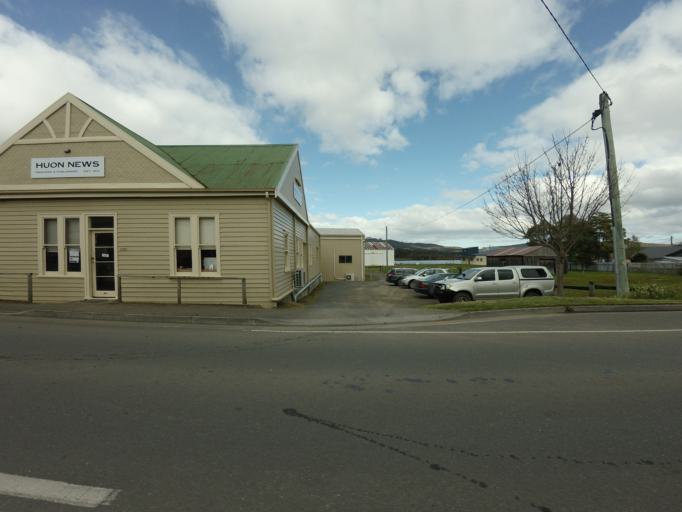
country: AU
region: Tasmania
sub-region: Huon Valley
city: Franklin
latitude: -43.0871
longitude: 147.0129
